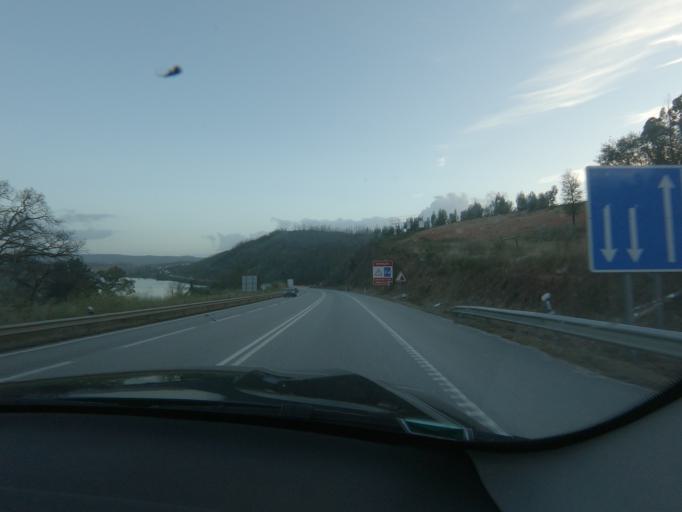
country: PT
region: Viseu
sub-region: Mortagua
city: Mortagua
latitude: 40.3370
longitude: -8.2245
